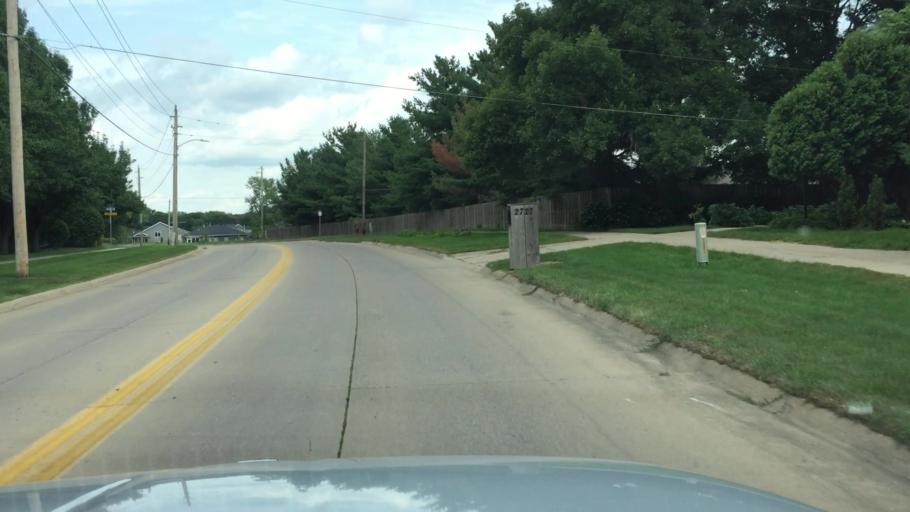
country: US
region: Iowa
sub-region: Johnson County
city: Iowa City
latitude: 41.6666
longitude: -91.4942
